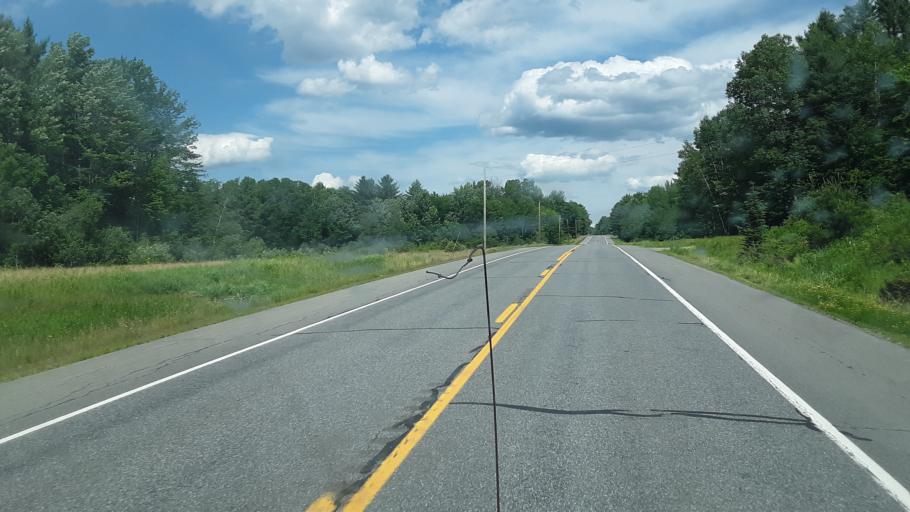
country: US
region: Maine
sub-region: Franklin County
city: New Sharon
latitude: 44.6473
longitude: -69.9744
